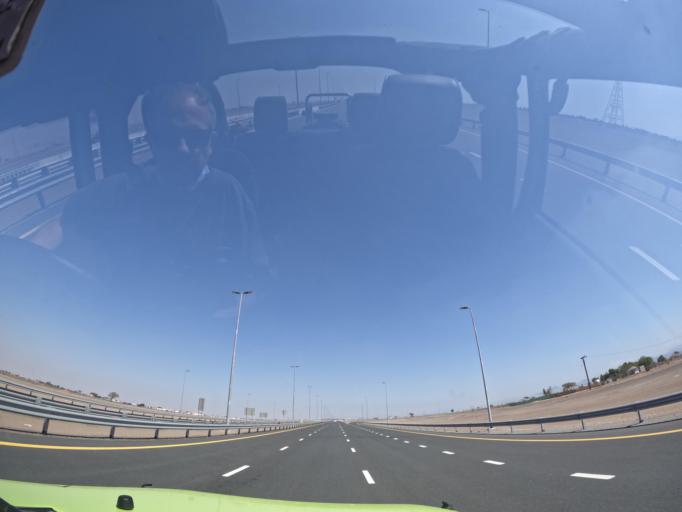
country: AE
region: Ash Shariqah
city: Adh Dhayd
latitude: 25.1032
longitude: 55.9295
